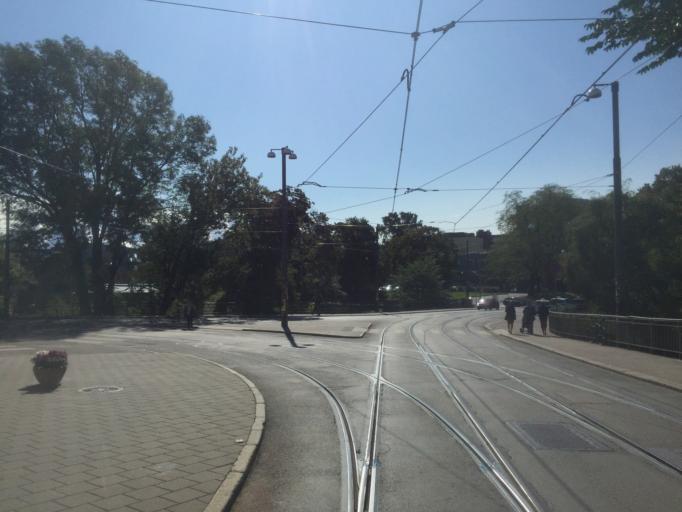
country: NO
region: Oslo
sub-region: Oslo
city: Oslo
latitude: 59.9182
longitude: 10.7593
